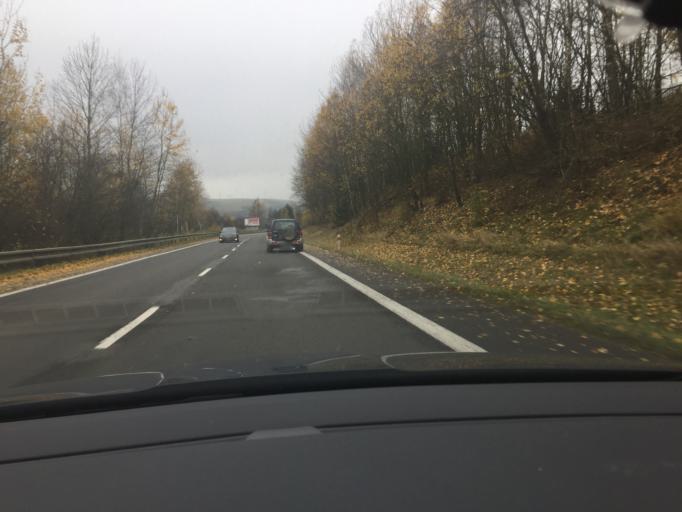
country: SK
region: Presovsky
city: Stara L'ubovna
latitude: 49.2977
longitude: 20.7111
